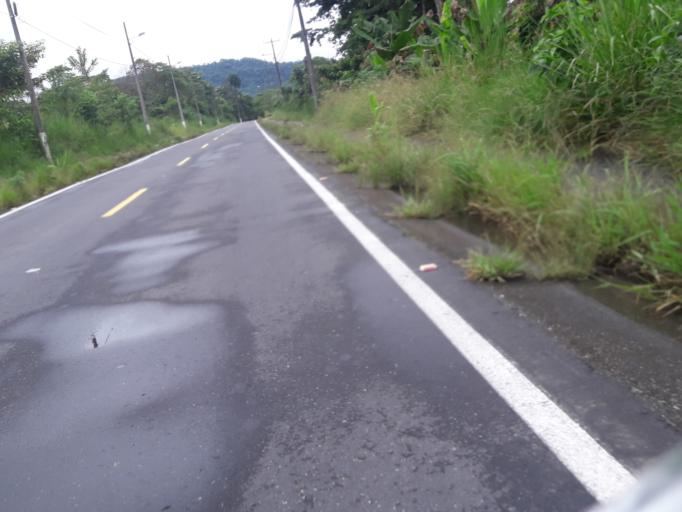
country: EC
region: Napo
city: Tena
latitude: -0.9743
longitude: -77.8545
